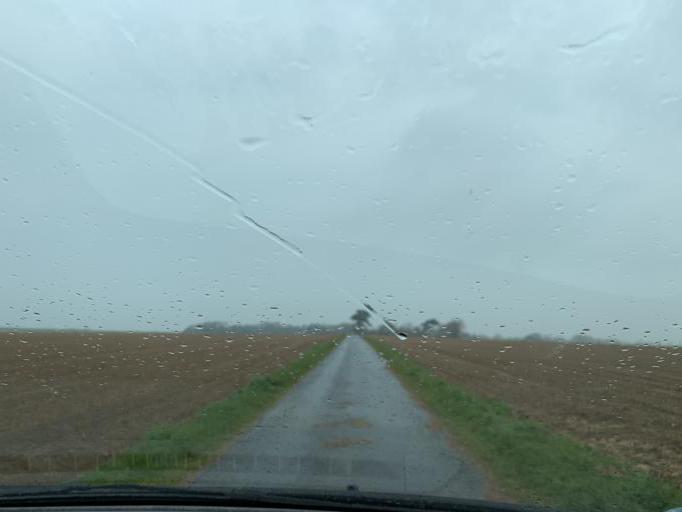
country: FR
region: Haute-Normandie
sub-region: Departement de la Seine-Maritime
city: Saint-Jouin-Bruneval
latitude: 49.6792
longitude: 0.1717
